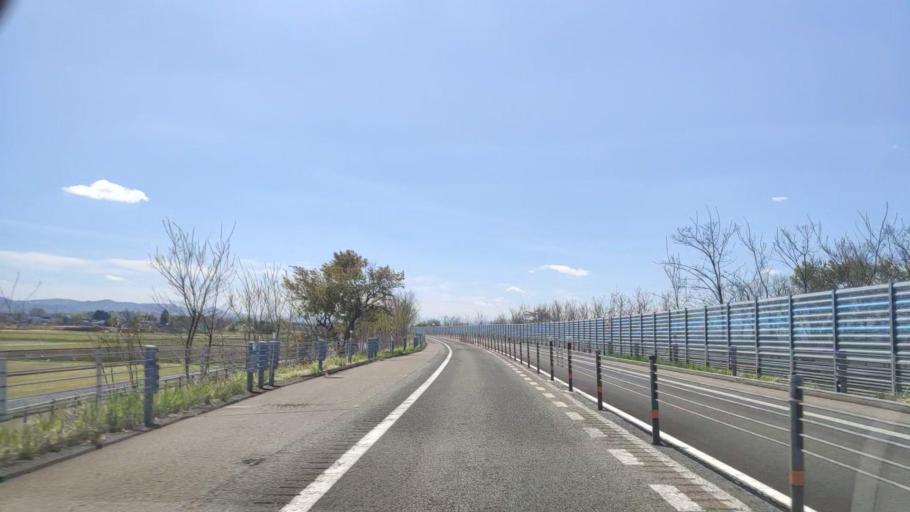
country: JP
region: Akita
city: Yokotemachi
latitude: 39.3400
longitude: 140.5012
